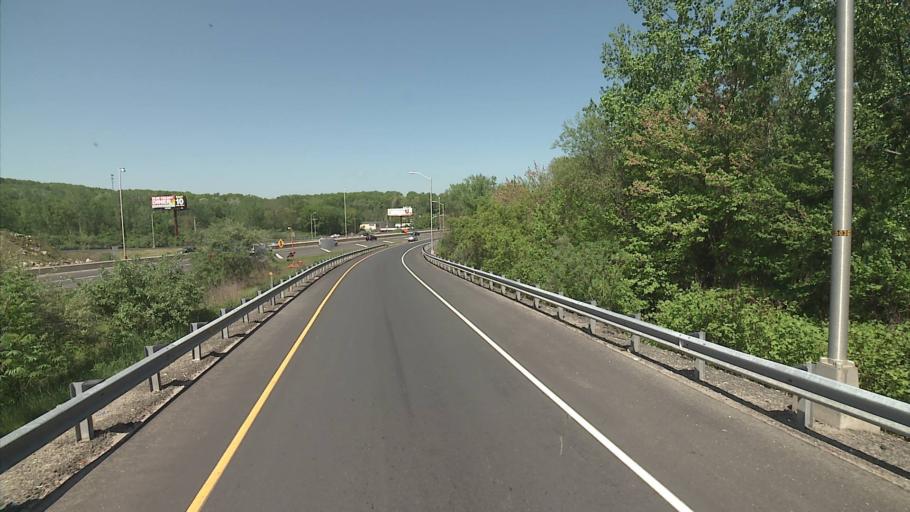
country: US
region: Connecticut
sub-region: New Haven County
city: Prospect
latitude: 41.5415
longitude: -72.9755
